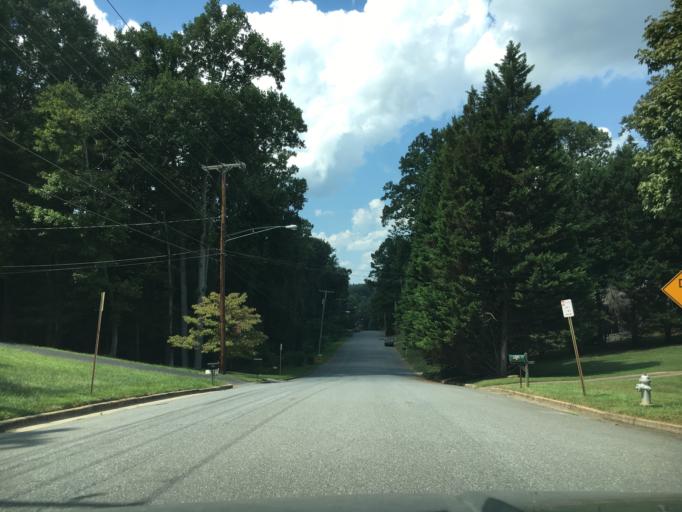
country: US
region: Virginia
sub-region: City of Lynchburg
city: West Lynchburg
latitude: 37.4200
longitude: -79.1711
